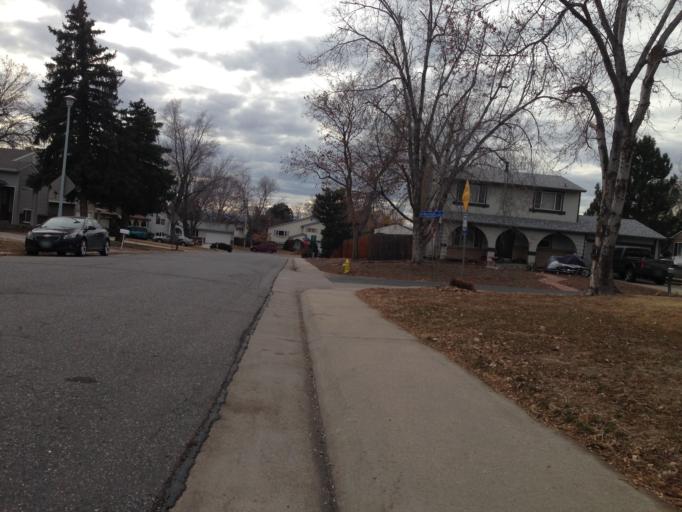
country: US
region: Colorado
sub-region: Adams County
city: Westminster
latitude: 39.8550
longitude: -105.0650
